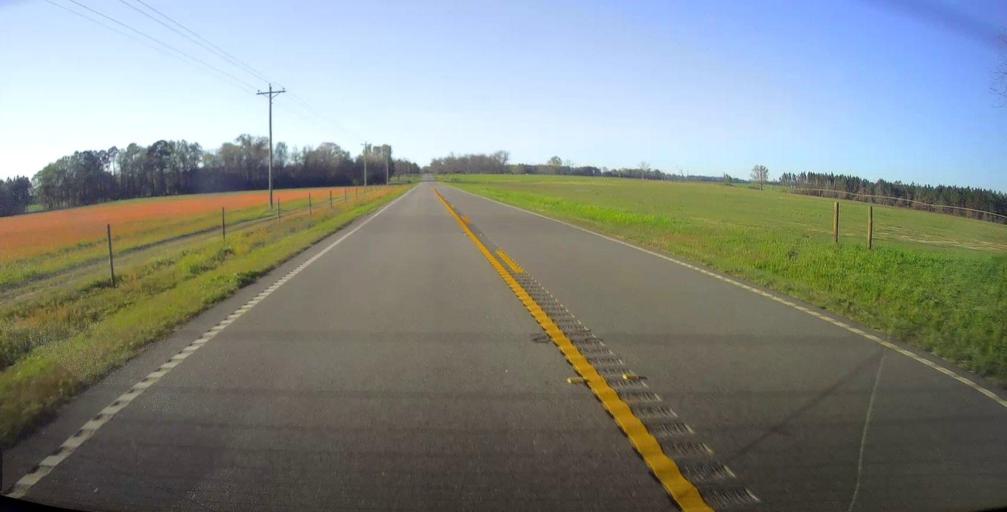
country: US
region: Georgia
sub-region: Wilcox County
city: Abbeville
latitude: 32.1474
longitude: -83.3473
